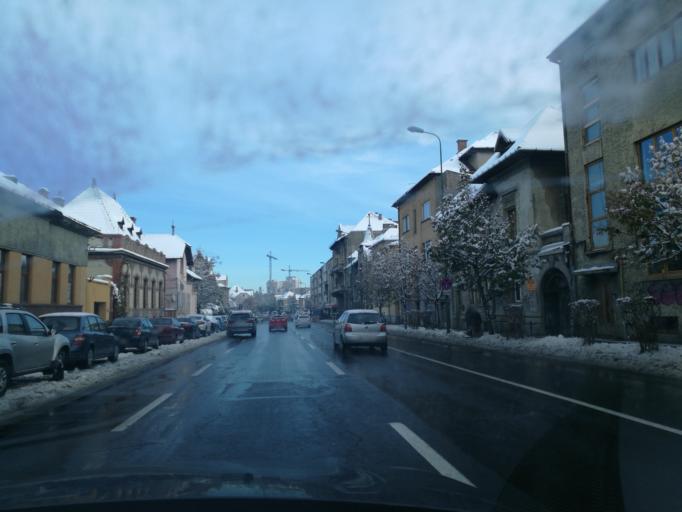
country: RO
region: Brasov
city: Brasov
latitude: 45.6470
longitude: 25.6017
